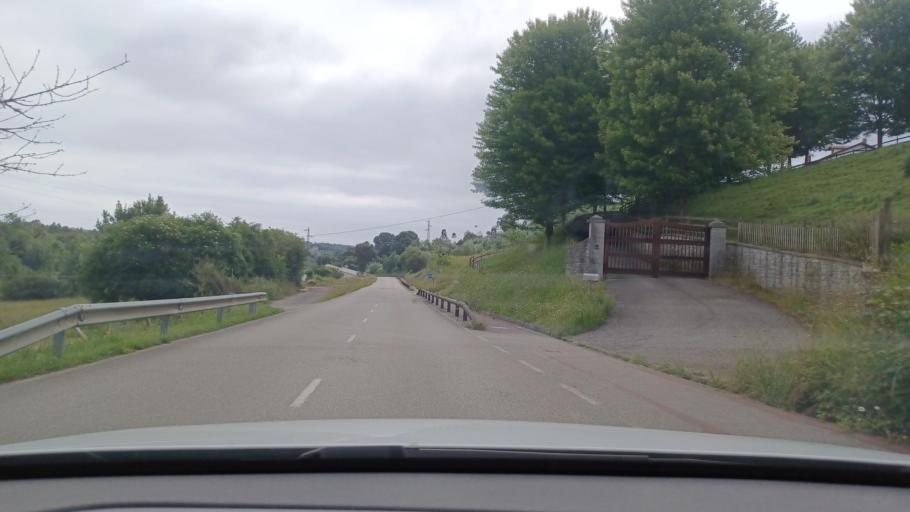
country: ES
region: Asturias
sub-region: Province of Asturias
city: Ribadesella
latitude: 43.4553
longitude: -5.0995
